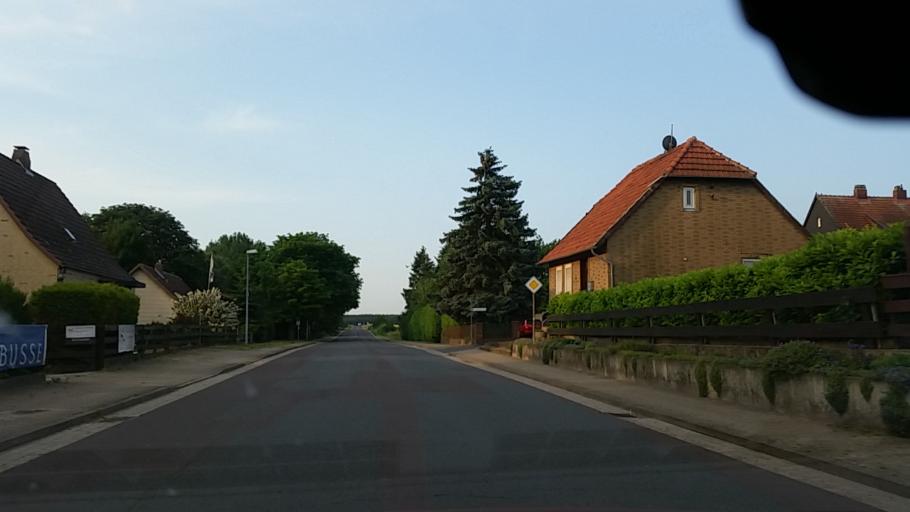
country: DE
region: Lower Saxony
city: Rennau
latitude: 52.2955
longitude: 10.9098
